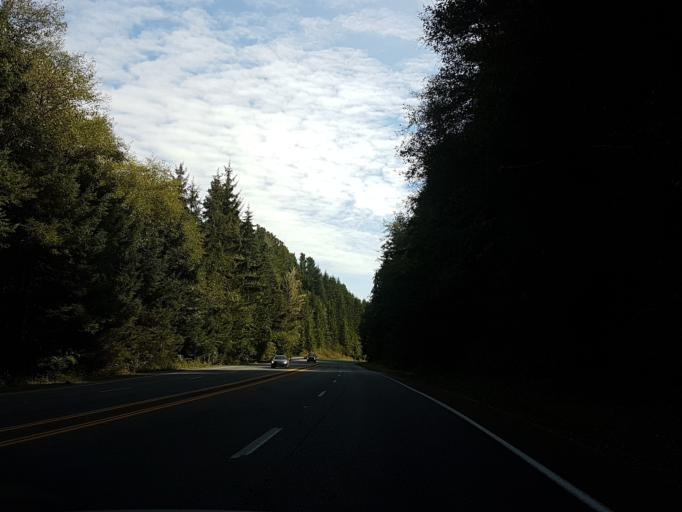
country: US
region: California
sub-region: Del Norte County
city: Bertsch-Oceanview
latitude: 41.4767
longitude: -124.0466
